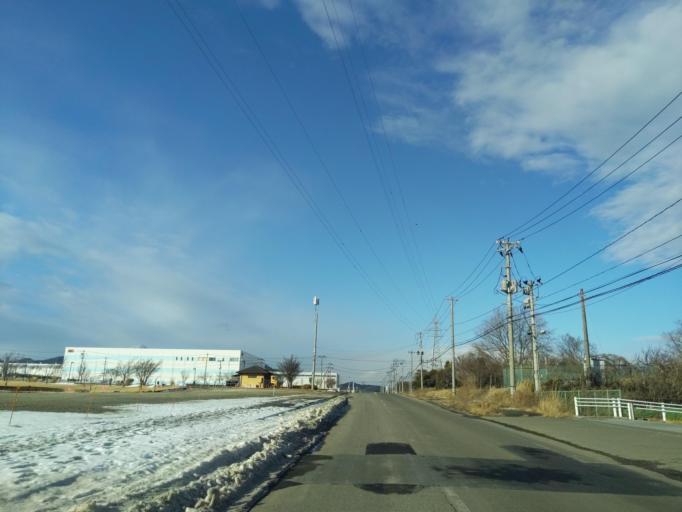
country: JP
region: Fukushima
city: Motomiya
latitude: 37.4770
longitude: 140.3742
